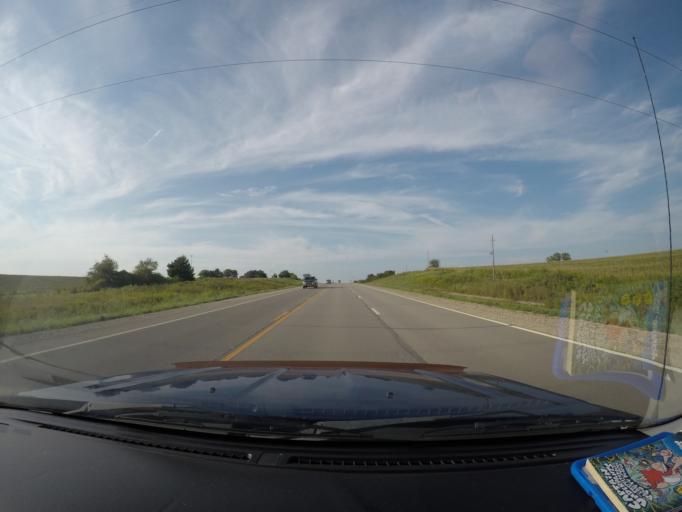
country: US
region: Kansas
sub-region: Atchison County
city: Atchison
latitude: 39.5274
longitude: -95.1329
